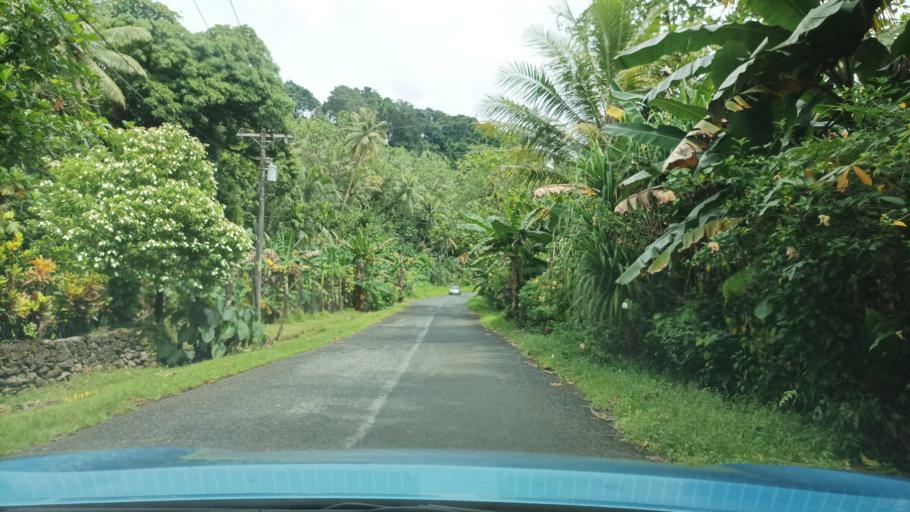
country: FM
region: Pohnpei
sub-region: Madolenihm Municipality
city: Madolenihm Municipality Government
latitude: 6.9008
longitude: 158.3175
